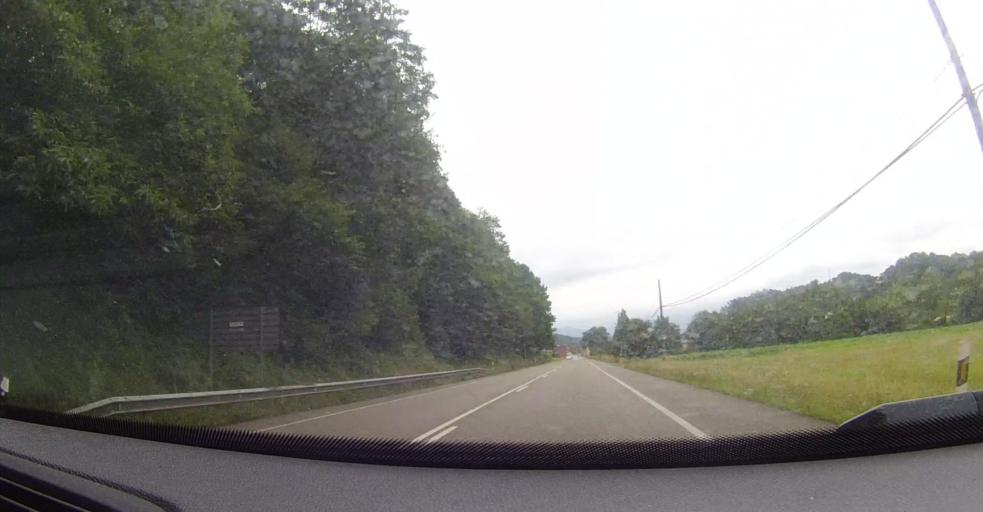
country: ES
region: Asturias
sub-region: Province of Asturias
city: Pilona
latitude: 43.3642
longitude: -5.2975
